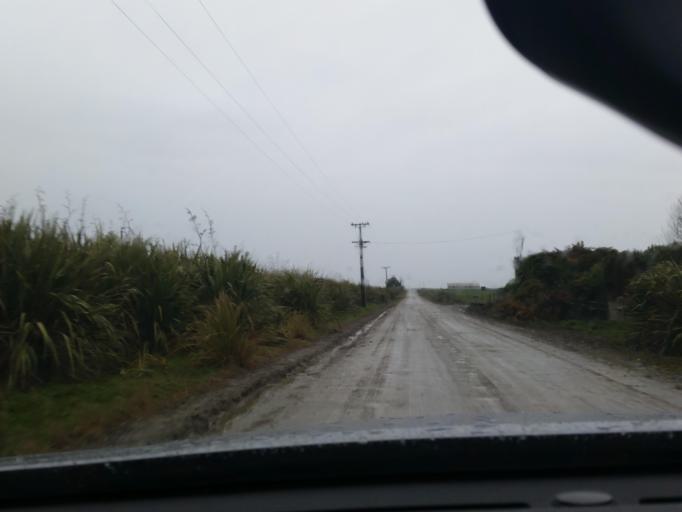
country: NZ
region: Southland
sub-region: Invercargill City
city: Invercargill
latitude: -46.4445
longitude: 168.5062
